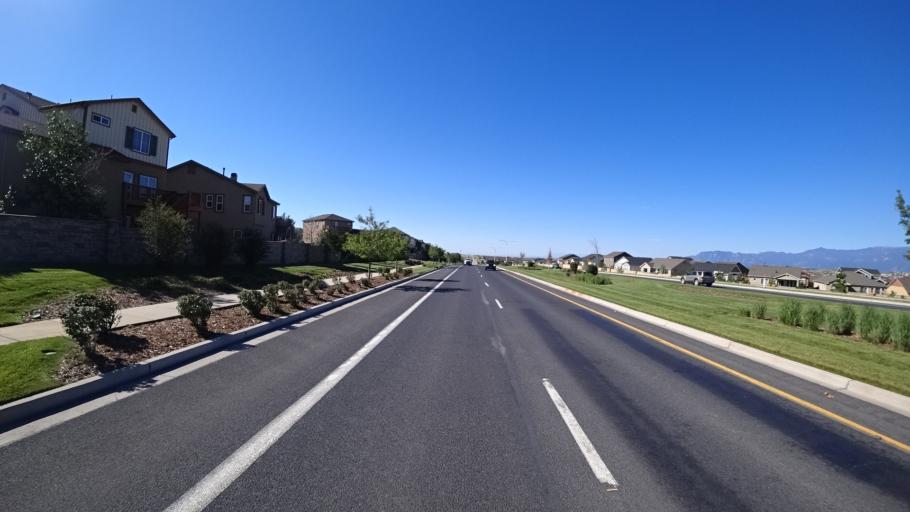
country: US
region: Colorado
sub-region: El Paso County
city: Cimarron Hills
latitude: 38.9322
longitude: -104.6827
